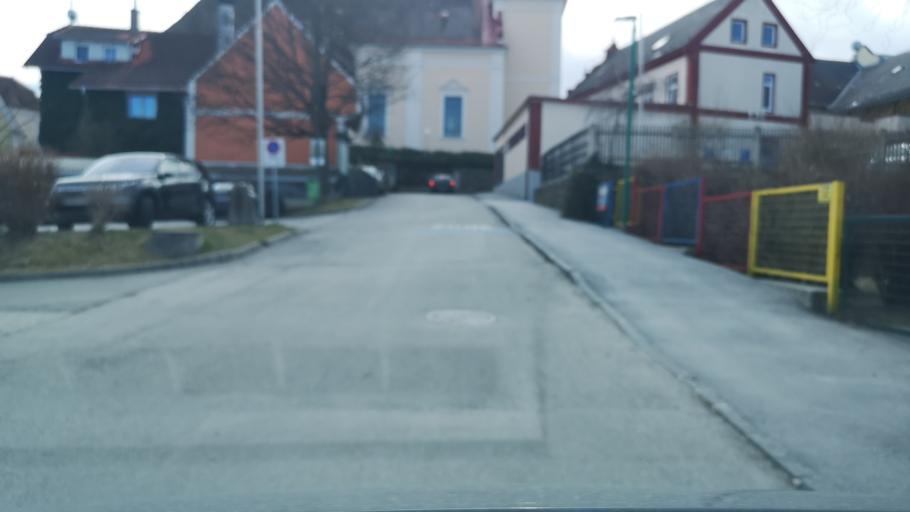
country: AT
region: Styria
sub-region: Politischer Bezirk Weiz
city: Birkfeld
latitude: 47.3556
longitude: 15.6951
